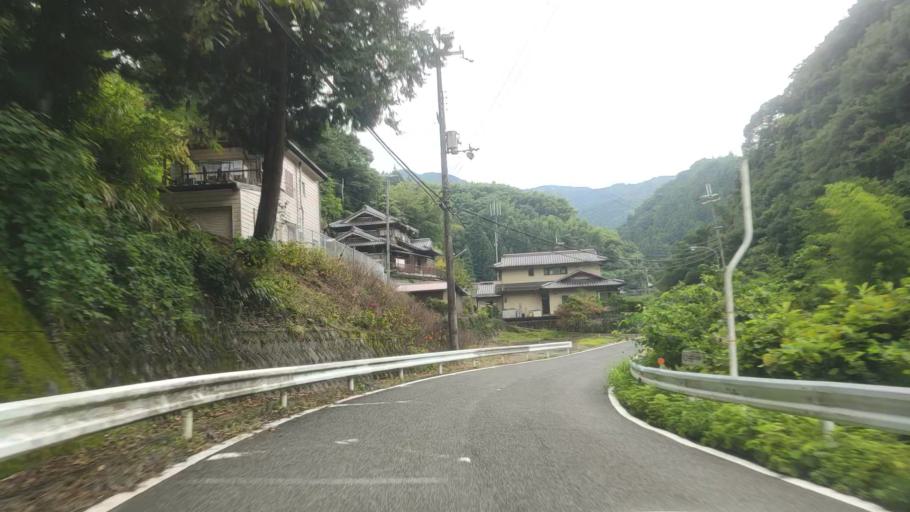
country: JP
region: Wakayama
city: Hashimoto
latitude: 34.2649
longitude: 135.5506
